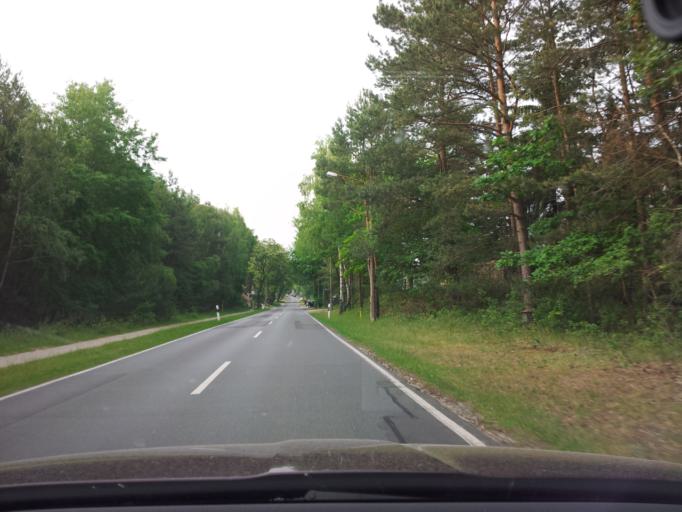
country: DE
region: Brandenburg
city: Fichtenwalde
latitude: 52.3049
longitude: 12.9300
